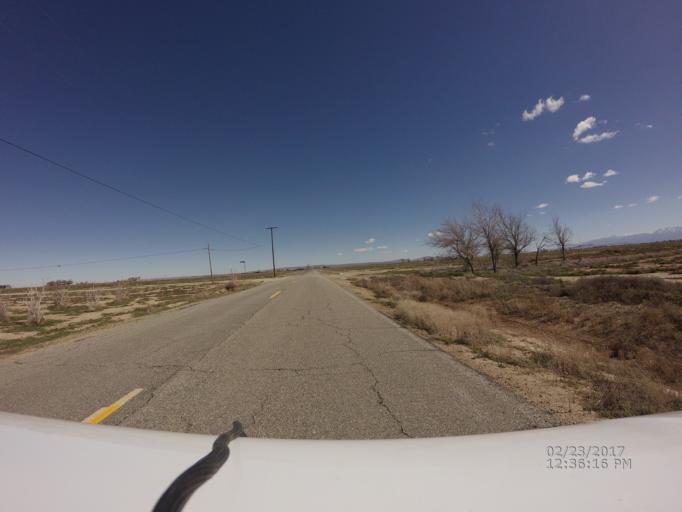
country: US
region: California
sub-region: Los Angeles County
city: Lancaster
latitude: 34.7486
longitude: -118.0149
